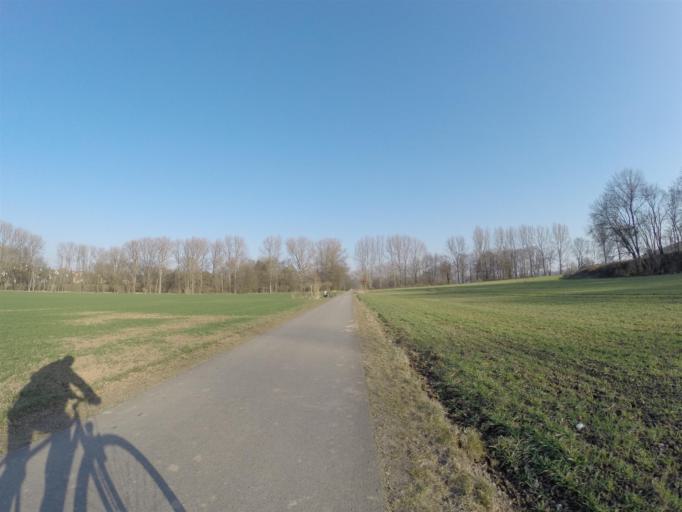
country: DE
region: Thuringia
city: Oettern
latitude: 50.9510
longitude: 11.3698
